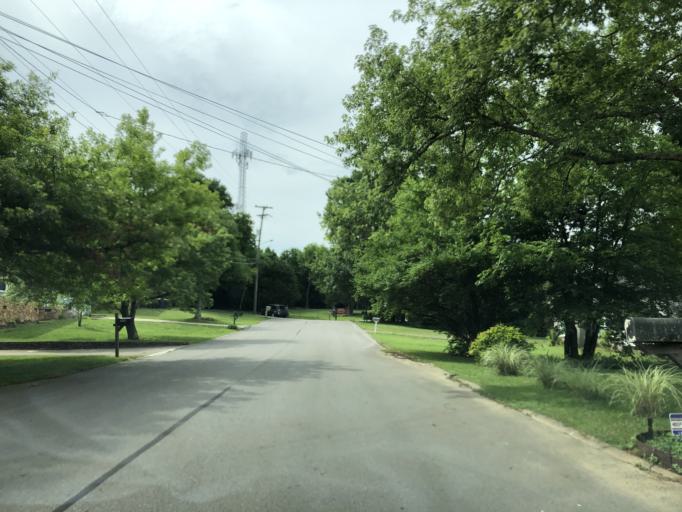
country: US
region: Tennessee
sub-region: Davidson County
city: Goodlettsville
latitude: 36.2810
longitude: -86.7155
